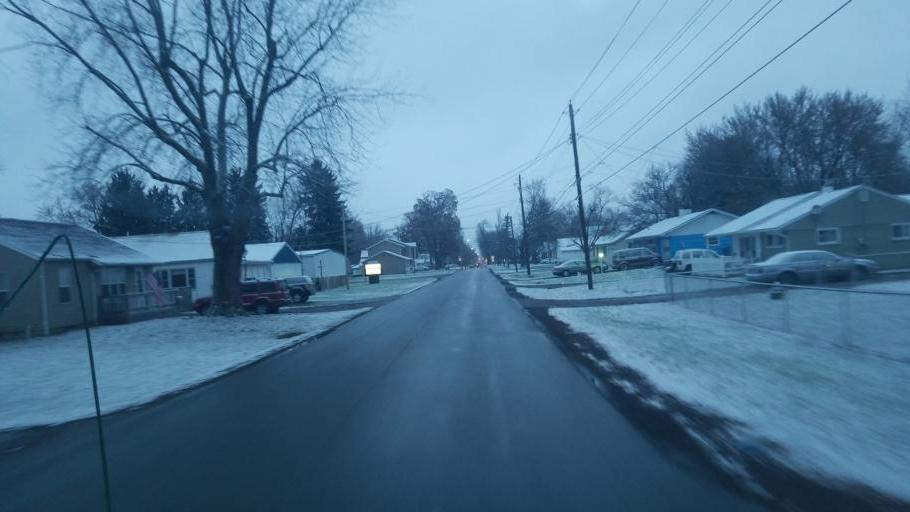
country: US
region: Ohio
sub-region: Marion County
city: Marion
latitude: 40.5837
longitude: -83.0977
